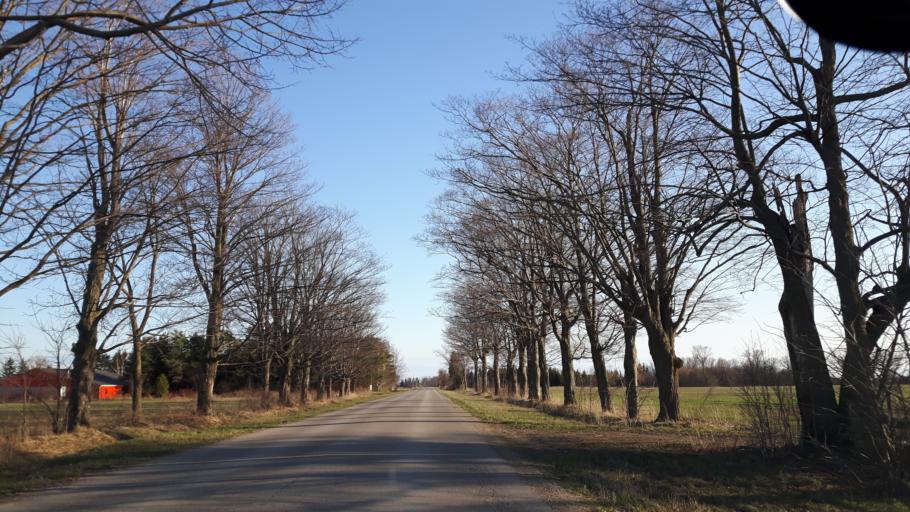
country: CA
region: Ontario
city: Goderich
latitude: 43.6540
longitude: -81.6846
